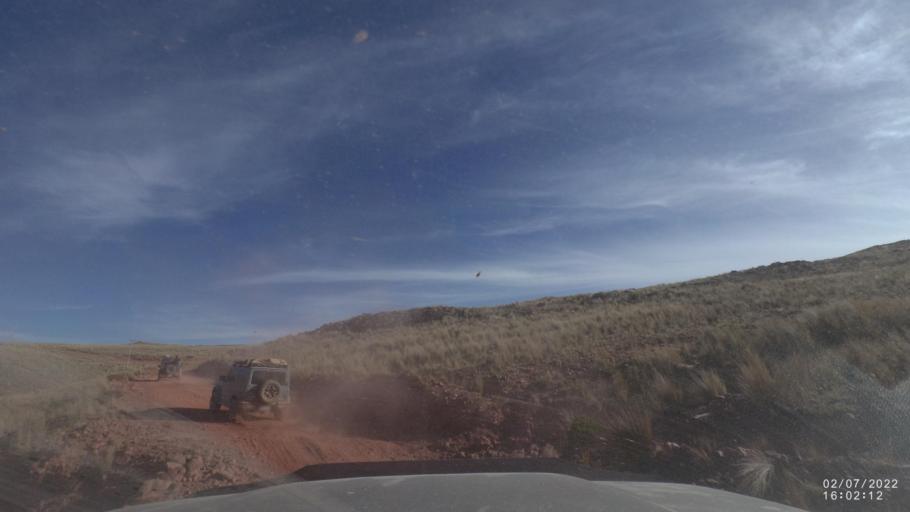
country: BO
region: Cochabamba
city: Irpa Irpa
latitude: -17.9089
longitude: -66.4404
